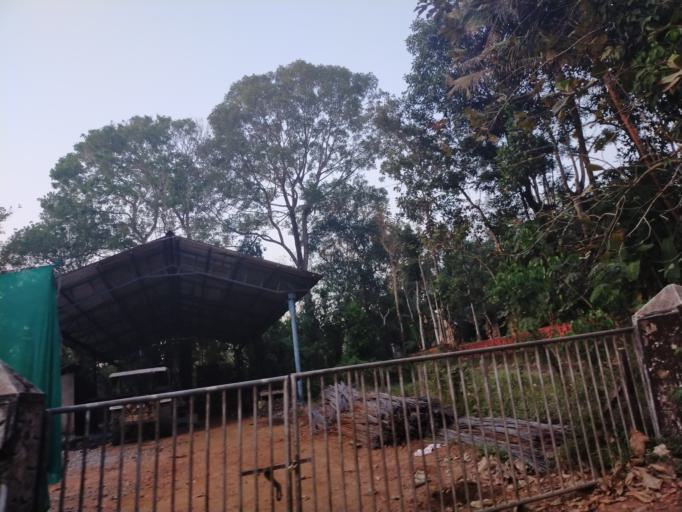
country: IN
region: Kerala
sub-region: Kottayam
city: Palackattumala
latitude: 9.7378
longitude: 76.5131
